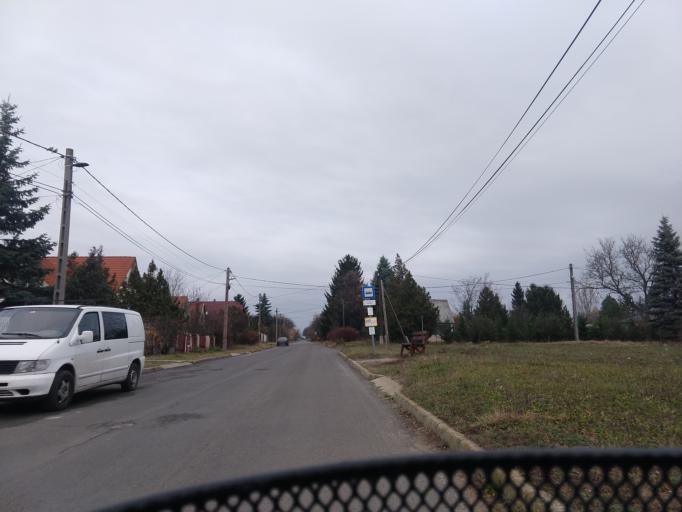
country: HU
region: Pest
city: Erdokertes
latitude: 47.6681
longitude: 19.2924
